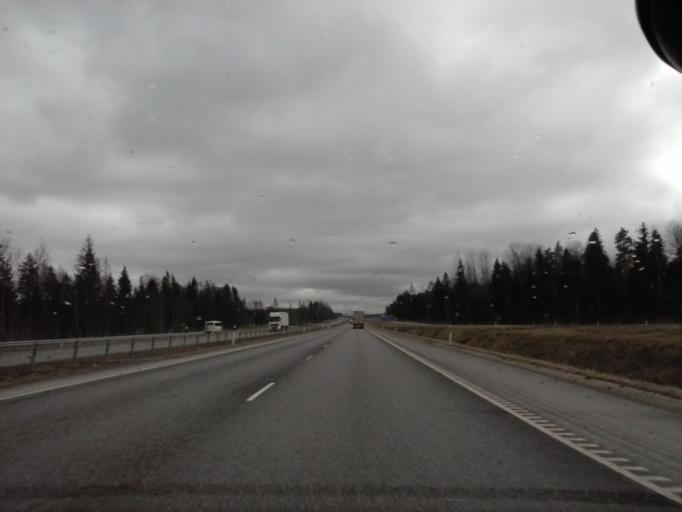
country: EE
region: Harju
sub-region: Rae vald
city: Vaida
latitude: 59.2306
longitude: 25.0315
